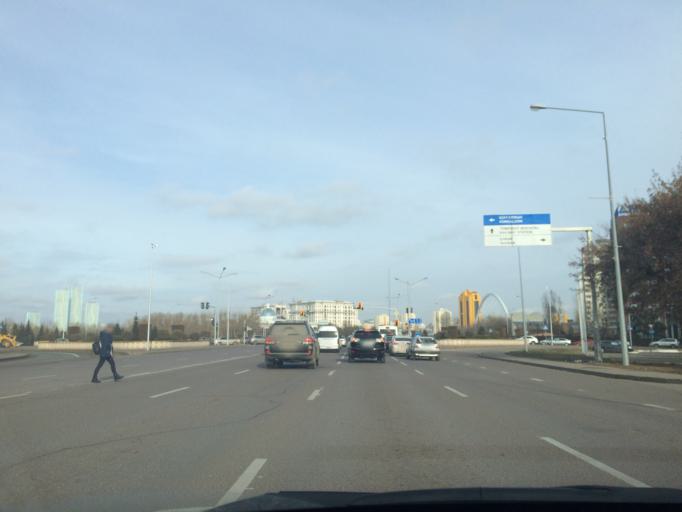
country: KZ
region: Astana Qalasy
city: Astana
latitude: 51.1462
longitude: 71.4220
